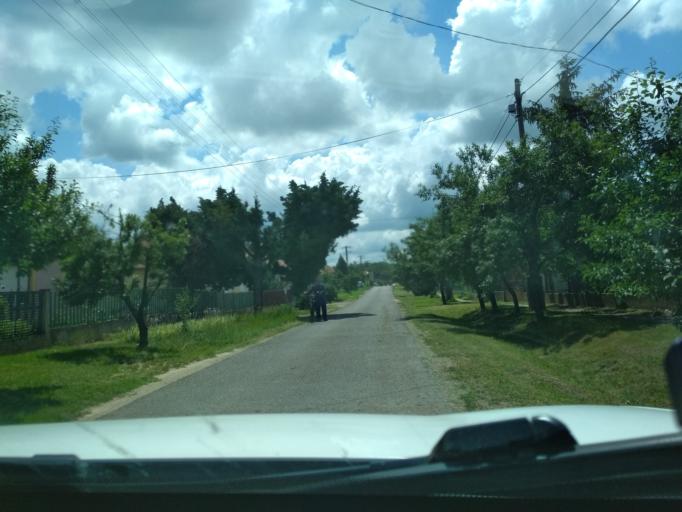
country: HU
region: Jasz-Nagykun-Szolnok
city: Tiszafured
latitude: 47.6079
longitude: 20.7772
